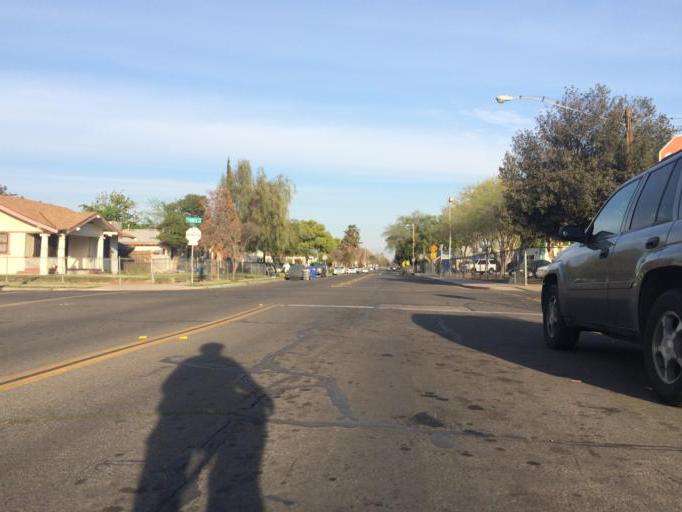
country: US
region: California
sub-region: Fresno County
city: Fresno
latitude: 36.7468
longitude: -119.7679
